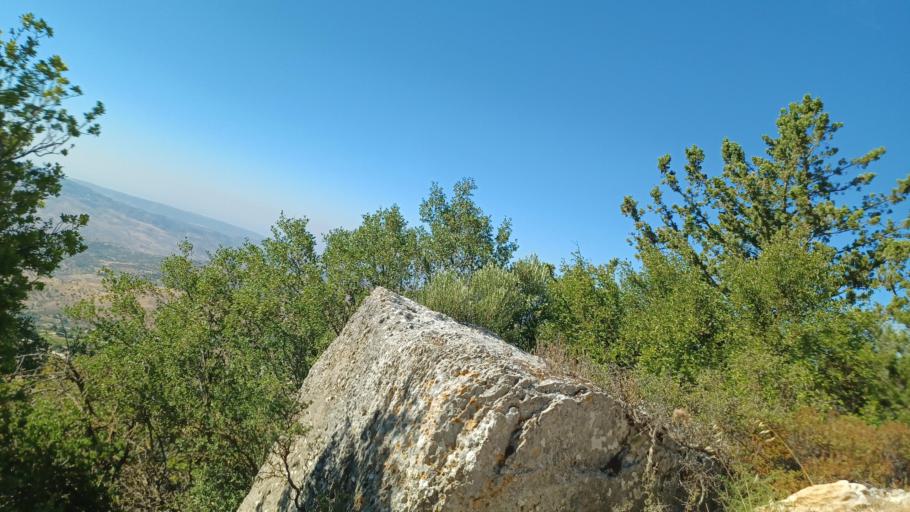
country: CY
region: Limassol
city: Pachna
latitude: 34.8982
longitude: 32.6404
